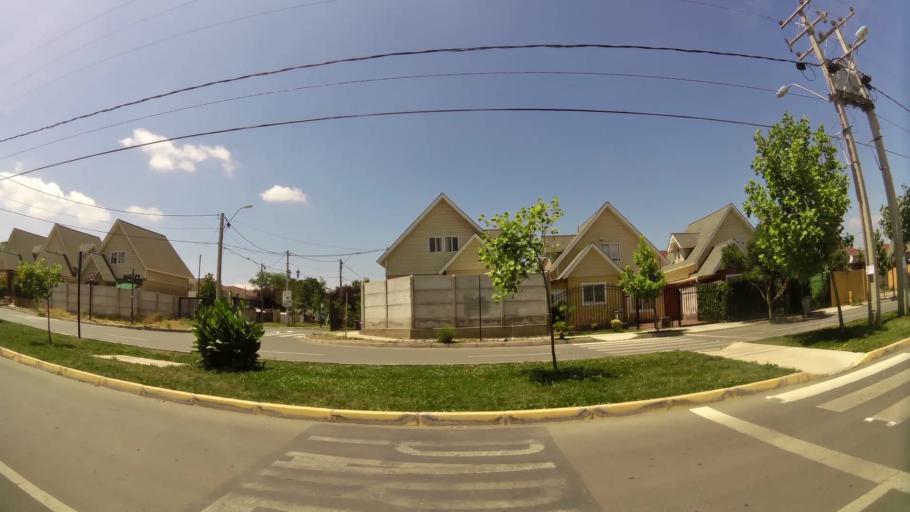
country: CL
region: Santiago Metropolitan
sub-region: Provincia de Talagante
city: Penaflor
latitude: -33.5695
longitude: -70.7923
